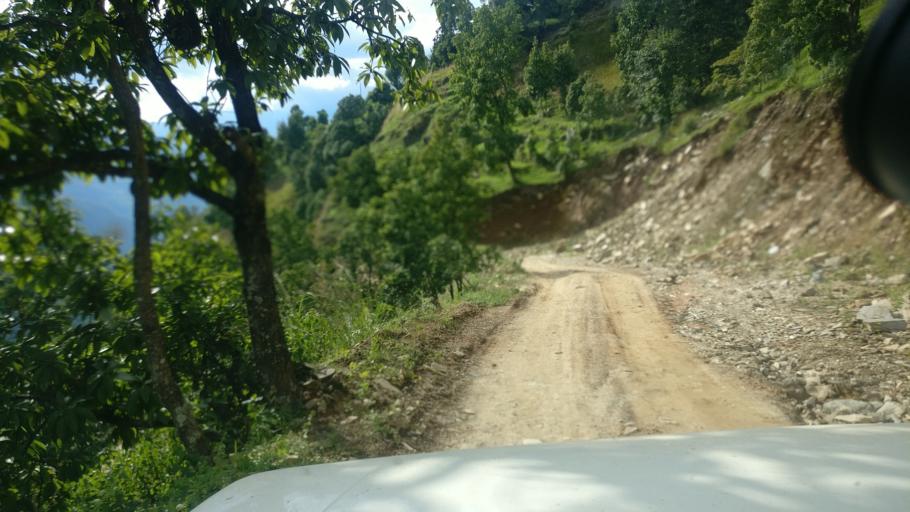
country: NP
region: Western Region
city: Baglung
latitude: 28.2647
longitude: 83.6458
